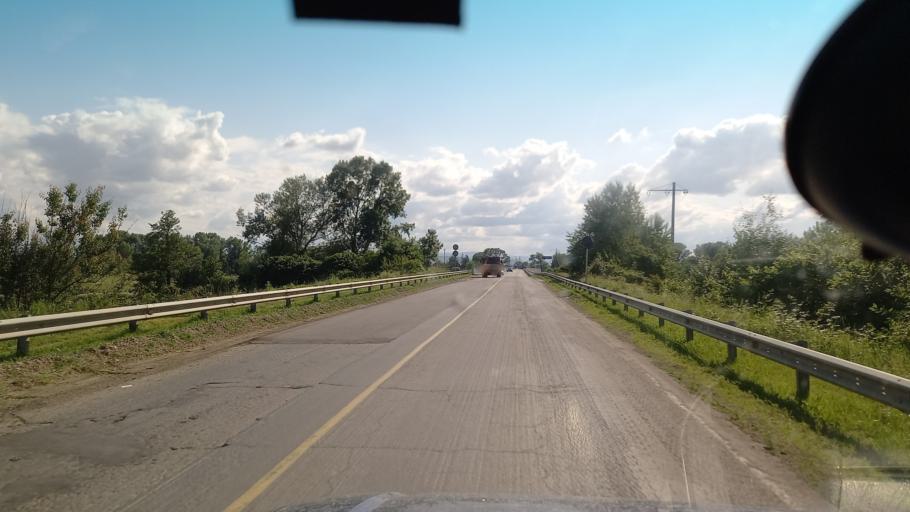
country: RU
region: Krasnodarskiy
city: Mostovskoy
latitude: 44.4012
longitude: 40.8243
